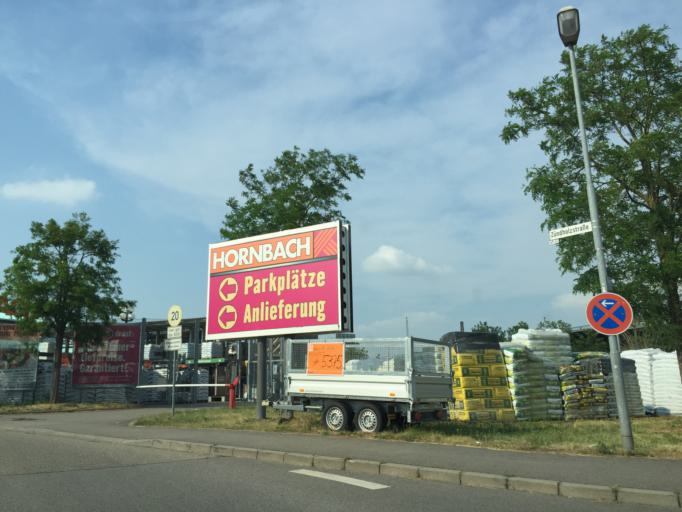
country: DE
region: Baden-Wuerttemberg
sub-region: Karlsruhe Region
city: Bruhl
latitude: 49.4128
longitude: 8.5469
